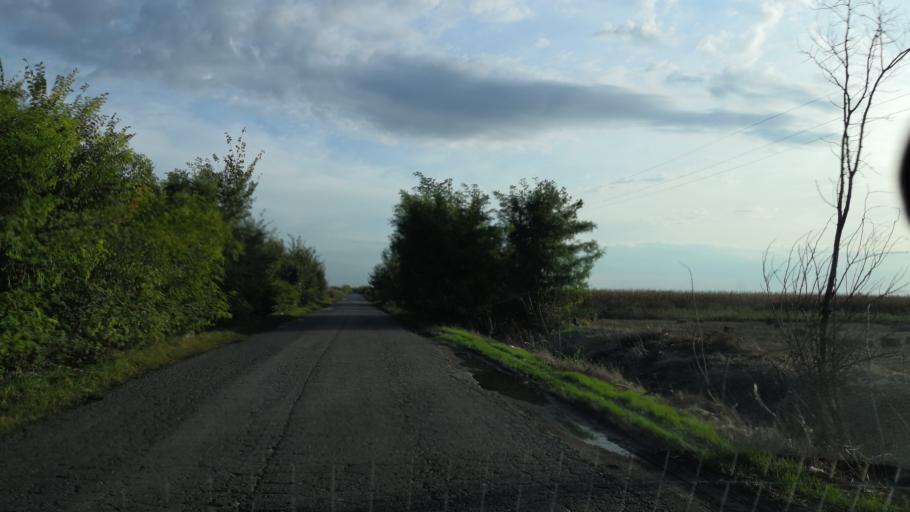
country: RS
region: Autonomna Pokrajina Vojvodina
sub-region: Sremski Okrug
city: Stara Pazova
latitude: 45.0074
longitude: 20.1666
